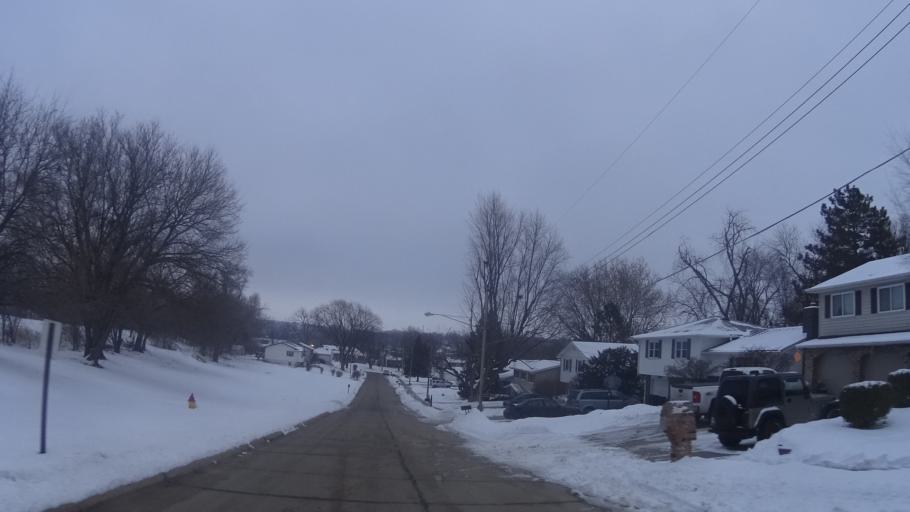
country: US
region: Nebraska
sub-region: Sarpy County
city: Offutt Air Force Base
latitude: 41.1505
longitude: -95.9241
